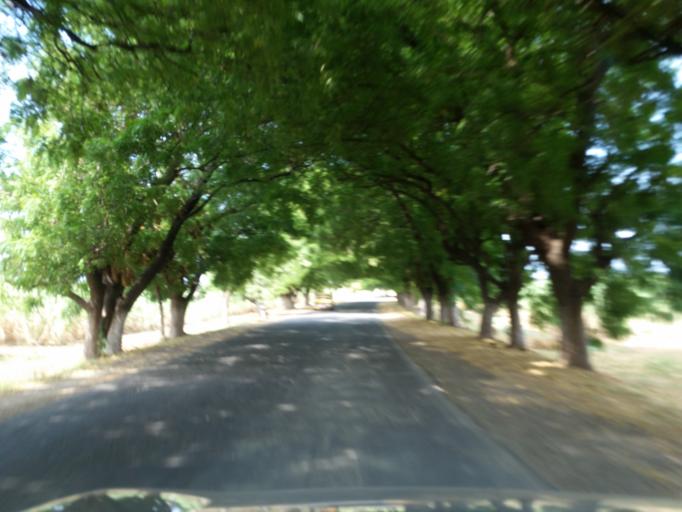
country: NI
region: Managua
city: Masachapa
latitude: 11.7904
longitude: -86.5061
